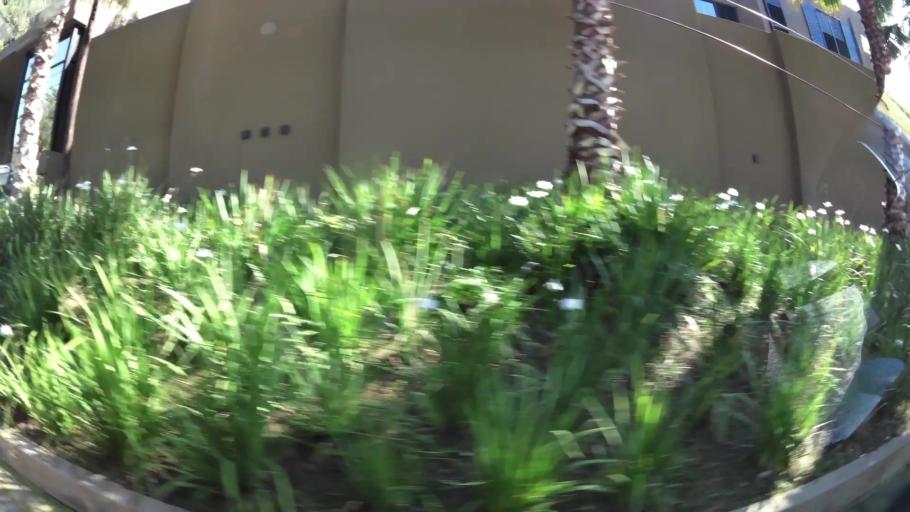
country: ZA
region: Gauteng
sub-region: City of Johannesburg Metropolitan Municipality
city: Johannesburg
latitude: -26.1128
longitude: 28.0397
